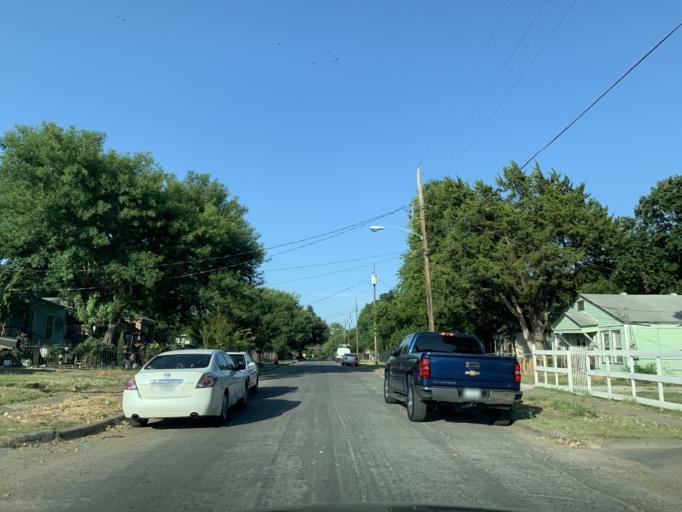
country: US
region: Texas
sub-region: Dallas County
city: Dallas
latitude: 32.7082
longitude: -96.7939
